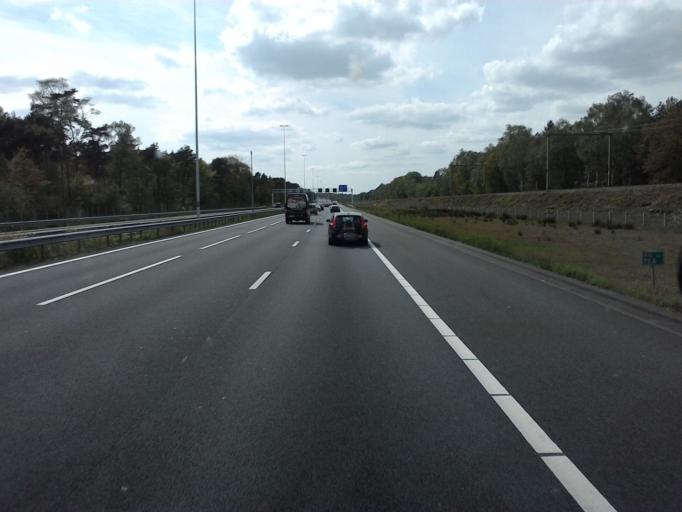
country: NL
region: Utrecht
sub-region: Gemeente Utrechtse Heuvelrug
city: Driebergen-Rijsenburg
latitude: 52.0653
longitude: 5.2975
